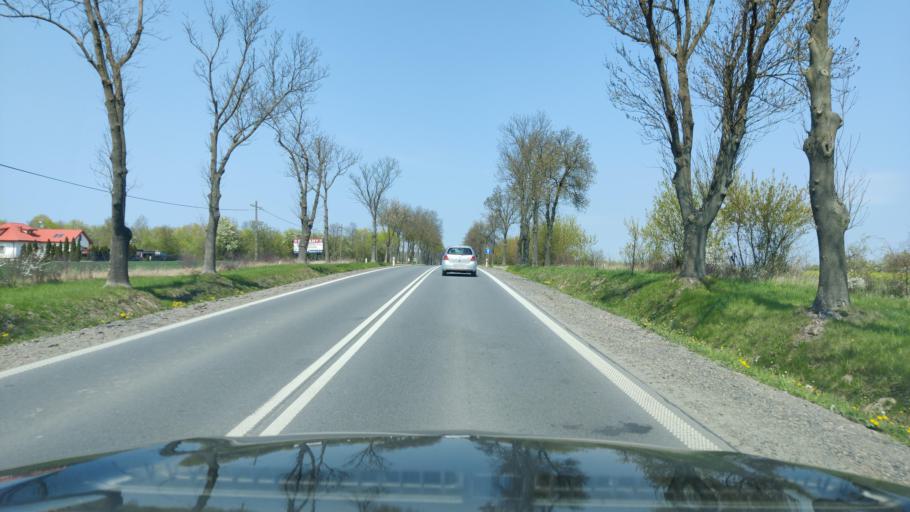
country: PL
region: Masovian Voivodeship
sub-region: Powiat pultuski
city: Pultusk
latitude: 52.6790
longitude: 21.0810
